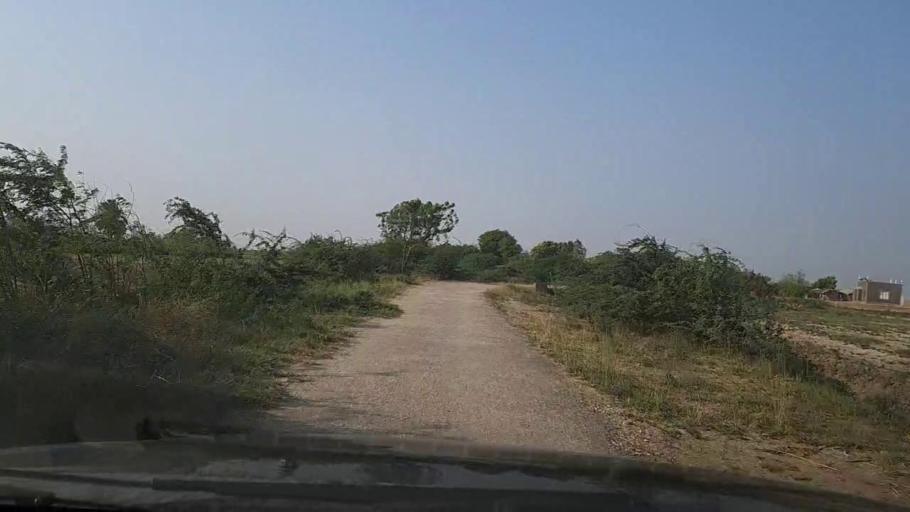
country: PK
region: Sindh
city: Mirpur Sakro
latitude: 24.6419
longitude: 67.7491
